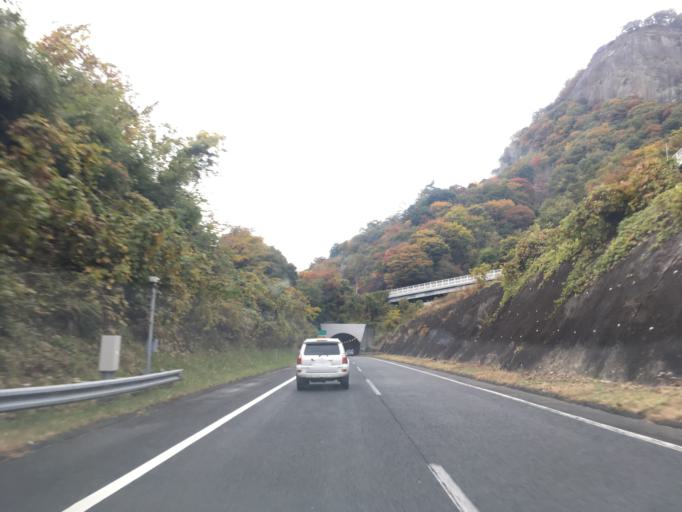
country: JP
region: Yamanashi
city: Otsuki
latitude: 35.6175
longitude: 138.9529
